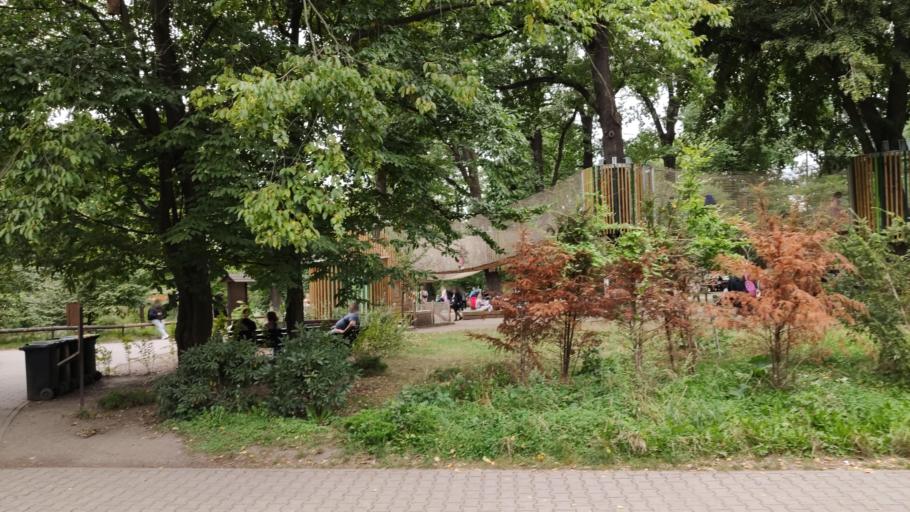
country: PL
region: Lower Silesian Voivodeship
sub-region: Powiat wroclawski
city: Wroclaw
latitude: 51.1020
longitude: 17.0771
